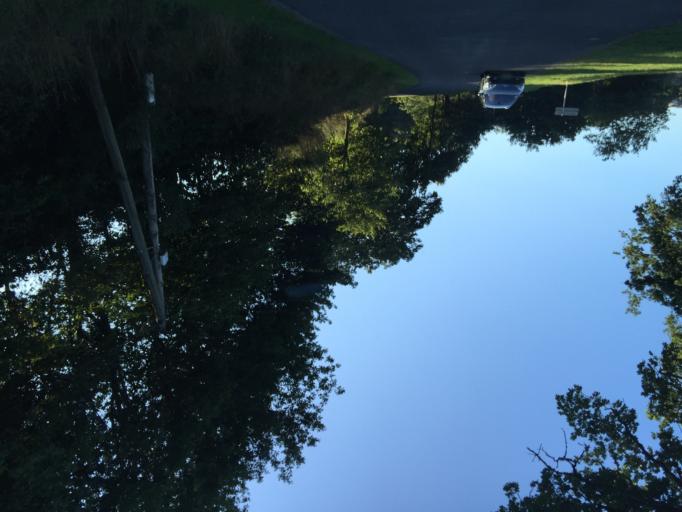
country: FR
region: Midi-Pyrenees
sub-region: Departement de l'Aveyron
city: Salles-Curan
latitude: 44.1926
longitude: 2.7887
